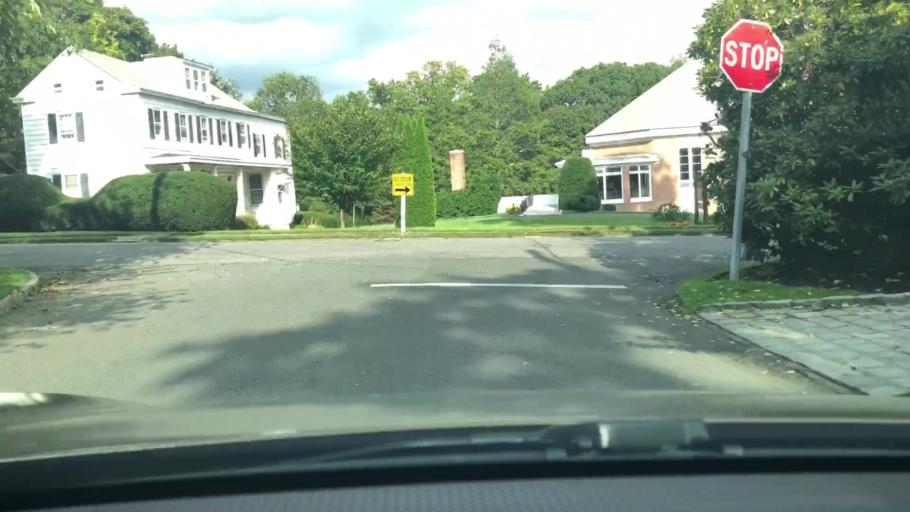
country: US
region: New York
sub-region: Westchester County
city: Bronxville
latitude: 40.9323
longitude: -73.8134
